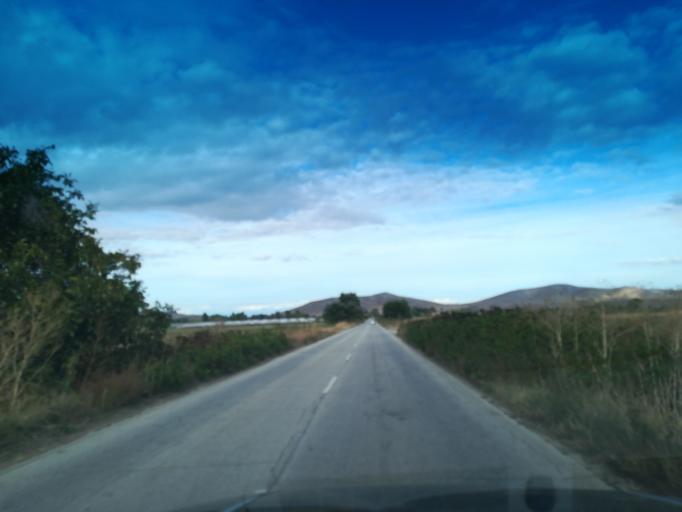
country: BG
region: Plovdiv
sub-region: Obshtina Krichim
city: Krichim
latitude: 42.0765
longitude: 24.4129
